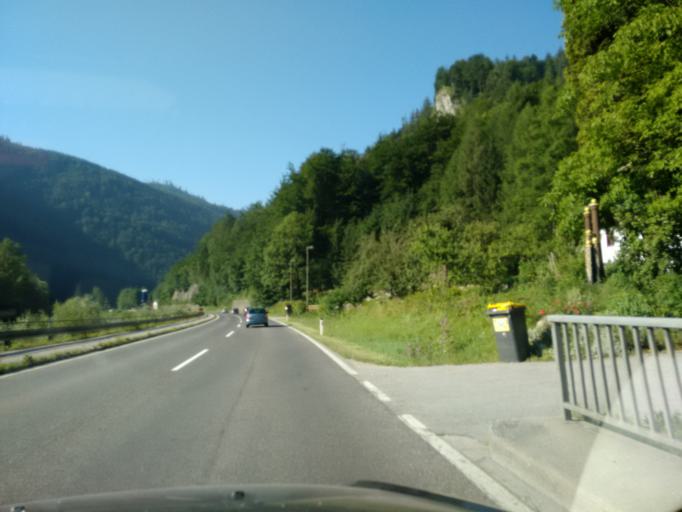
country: AT
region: Upper Austria
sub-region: Politischer Bezirk Gmunden
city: Bad Ischl
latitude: 47.7359
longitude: 13.6579
